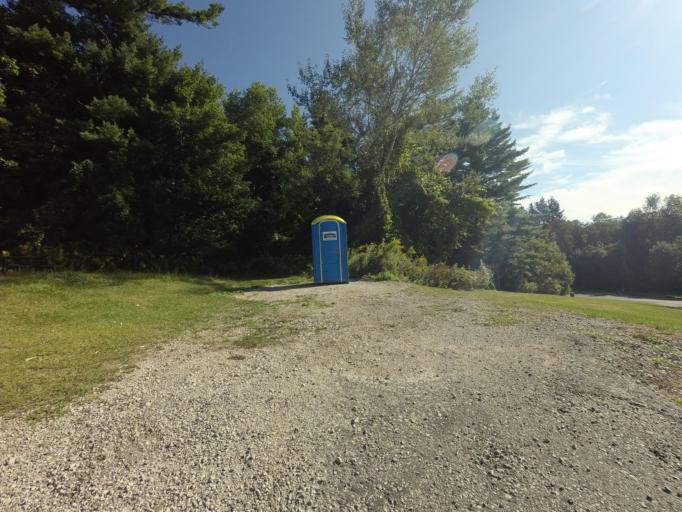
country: CA
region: Ontario
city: Waterloo
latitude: 43.6794
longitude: -80.4422
